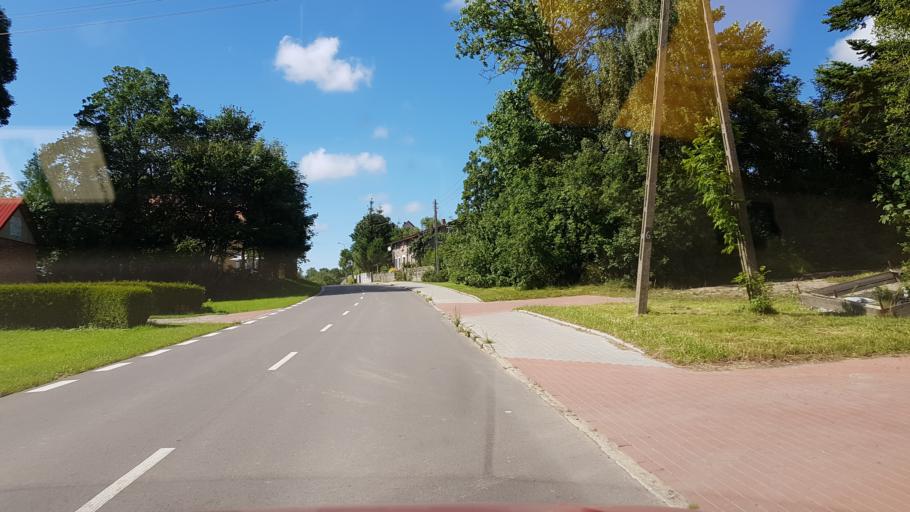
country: PL
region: West Pomeranian Voivodeship
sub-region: Powiat bialogardzki
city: Karlino
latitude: 54.1883
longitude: 15.9153
